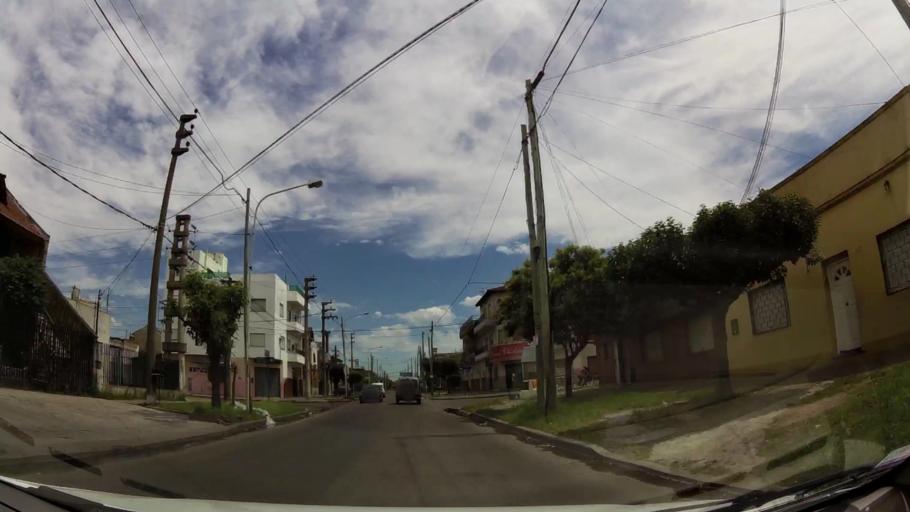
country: AR
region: Buenos Aires
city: San Justo
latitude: -34.6838
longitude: -58.5269
